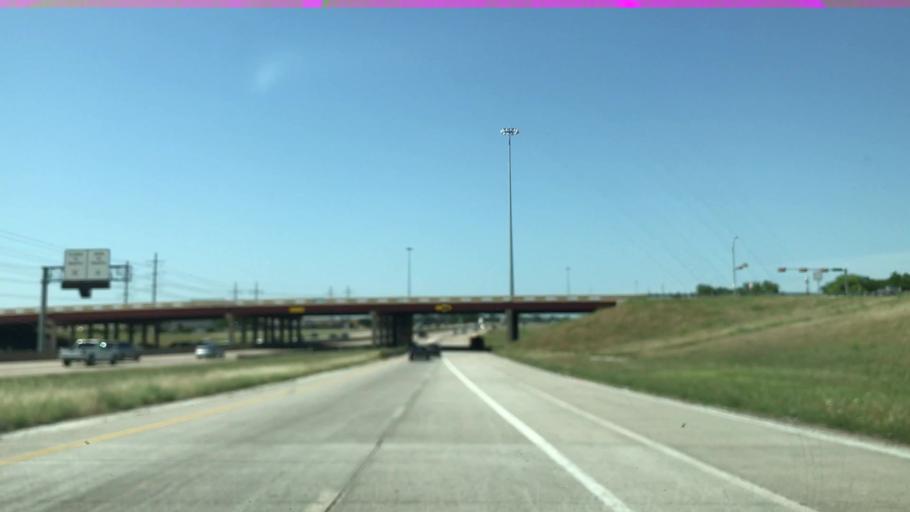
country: US
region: Texas
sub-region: Tarrant County
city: Euless
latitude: 32.8440
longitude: -97.0163
